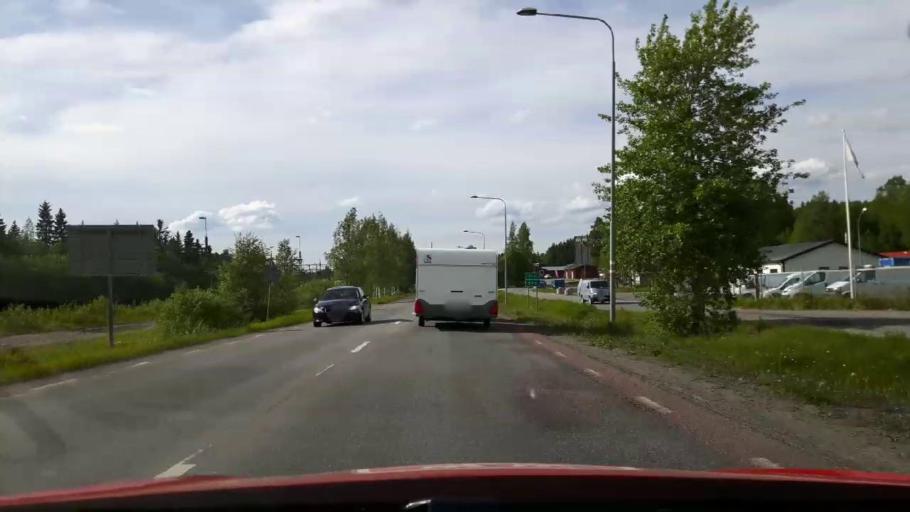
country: SE
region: Jaemtland
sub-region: OEstersunds Kommun
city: Brunflo
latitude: 63.0786
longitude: 14.8281
